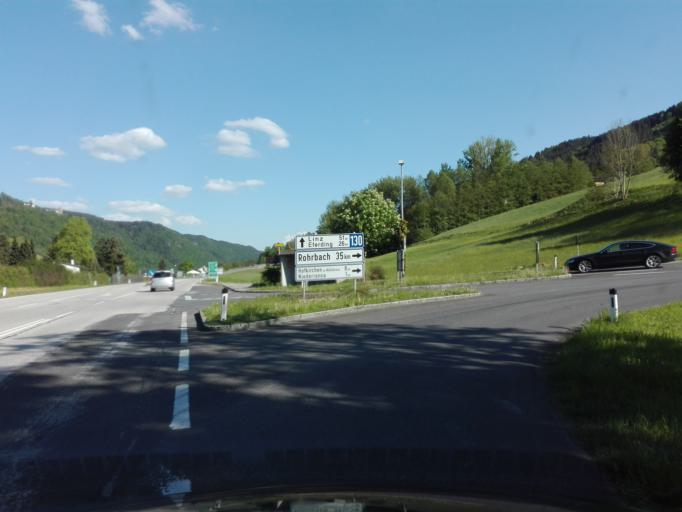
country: AT
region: Upper Austria
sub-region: Politischer Bezirk Rohrbach
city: Pfarrkirchen im Muehlkreis
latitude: 48.4636
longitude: 13.7986
